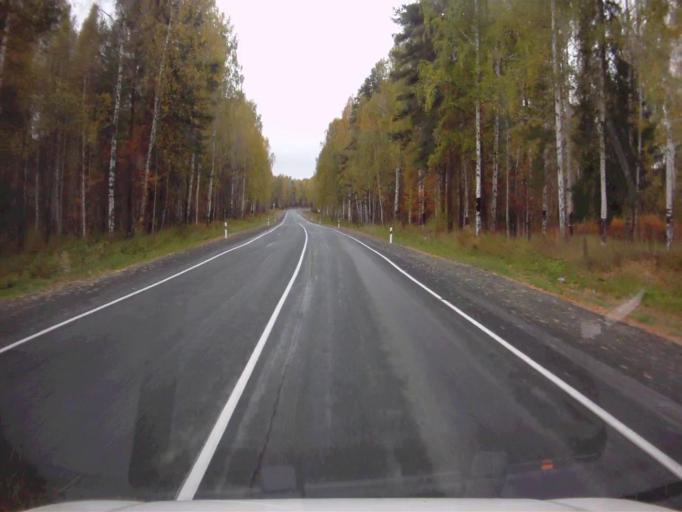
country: RU
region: Chelyabinsk
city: Nyazepetrovsk
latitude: 56.0632
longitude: 59.7250
